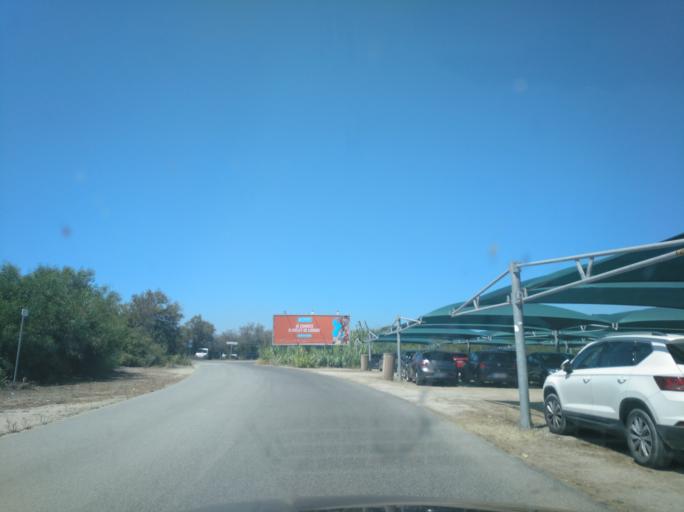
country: PT
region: Setubal
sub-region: Almada
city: Costa de Caparica
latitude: 38.6598
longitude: -9.2520
